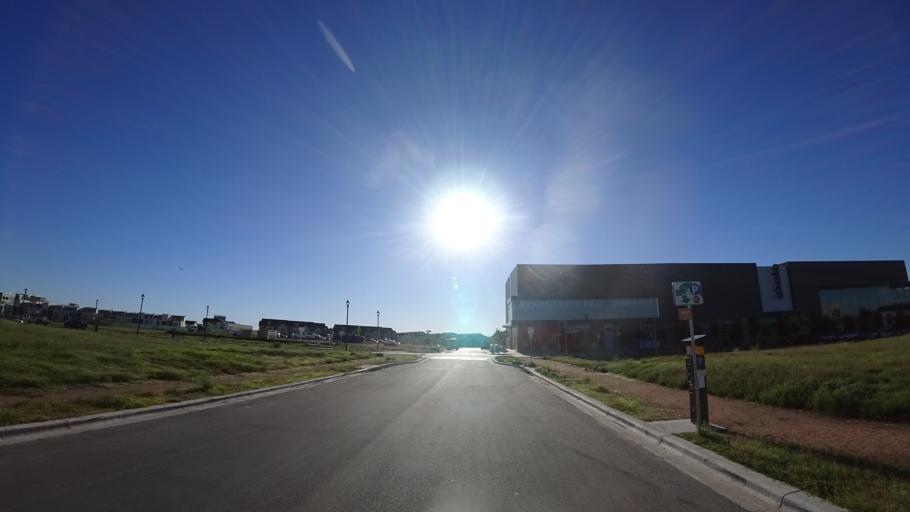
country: US
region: Texas
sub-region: Travis County
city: Austin
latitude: 30.2995
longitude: -97.7048
